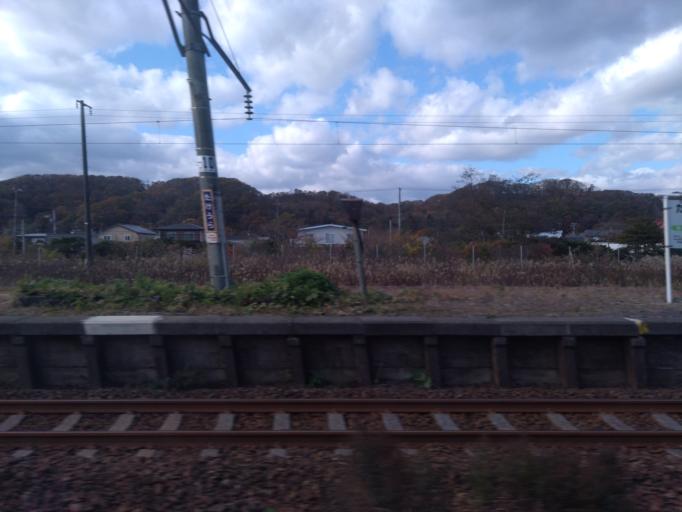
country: JP
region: Hokkaido
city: Shiraoi
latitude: 42.4927
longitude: 141.2600
